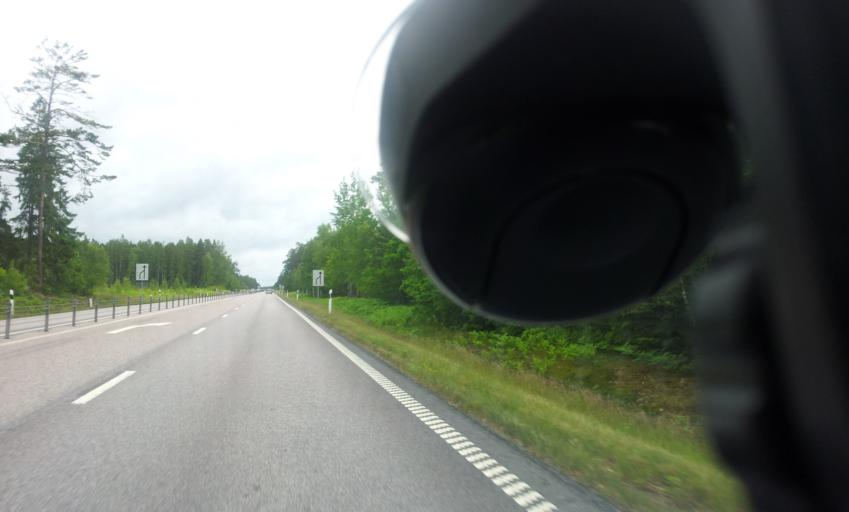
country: SE
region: Kalmar
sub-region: Monsteras Kommun
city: Timmernabben
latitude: 57.0015
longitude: 16.4174
